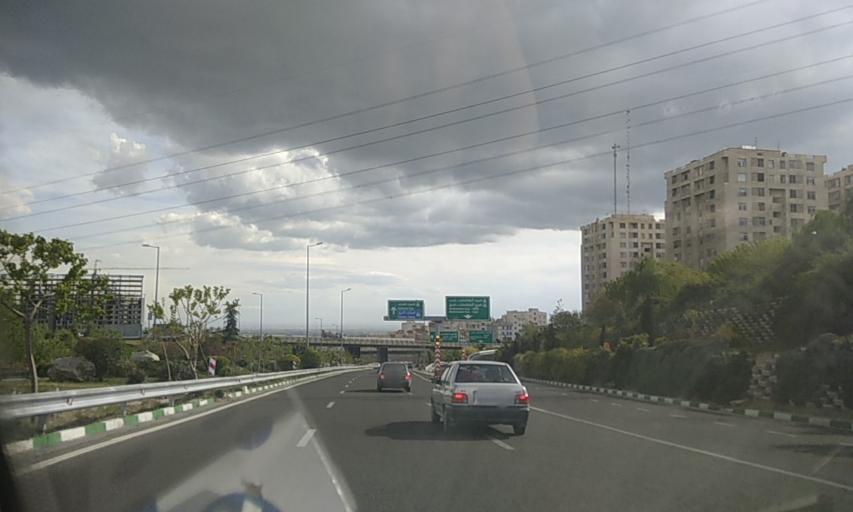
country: IR
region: Tehran
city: Tajrish
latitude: 35.7658
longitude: 51.2978
